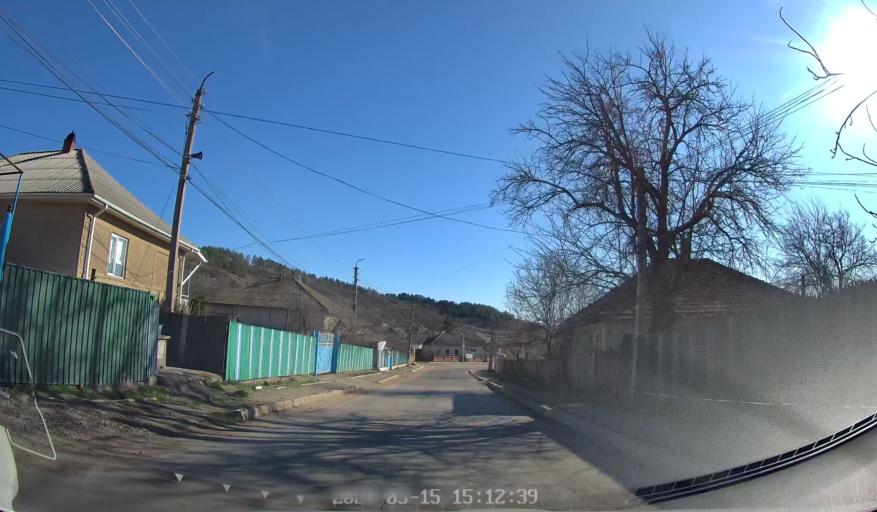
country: MD
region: Orhei
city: Orhei
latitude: 47.2537
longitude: 28.7739
